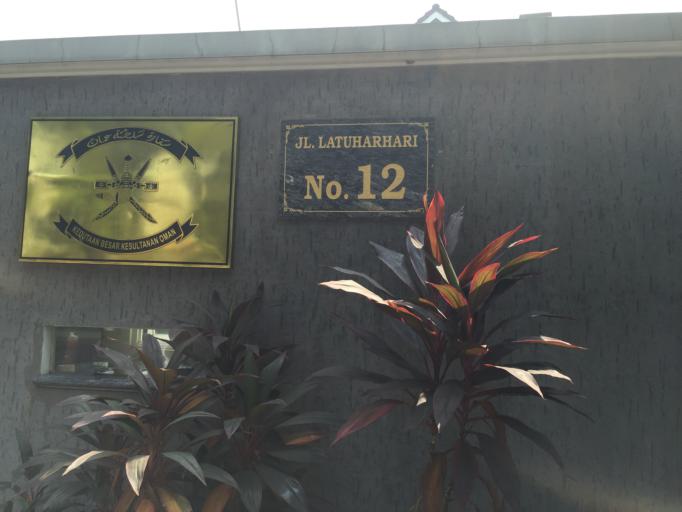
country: ID
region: Jakarta Raya
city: Jakarta
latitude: -6.2051
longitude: 106.8379
